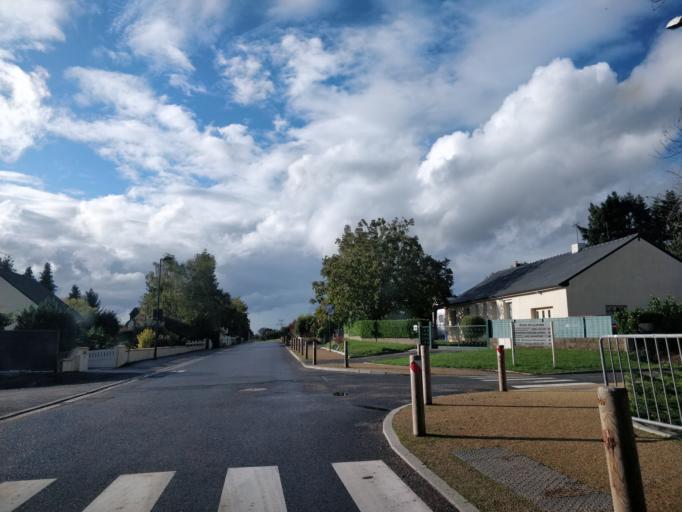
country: FR
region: Brittany
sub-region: Departement d'Ille-et-Vilaine
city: Servon-sur-Vilaine
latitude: 48.1245
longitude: -1.4673
